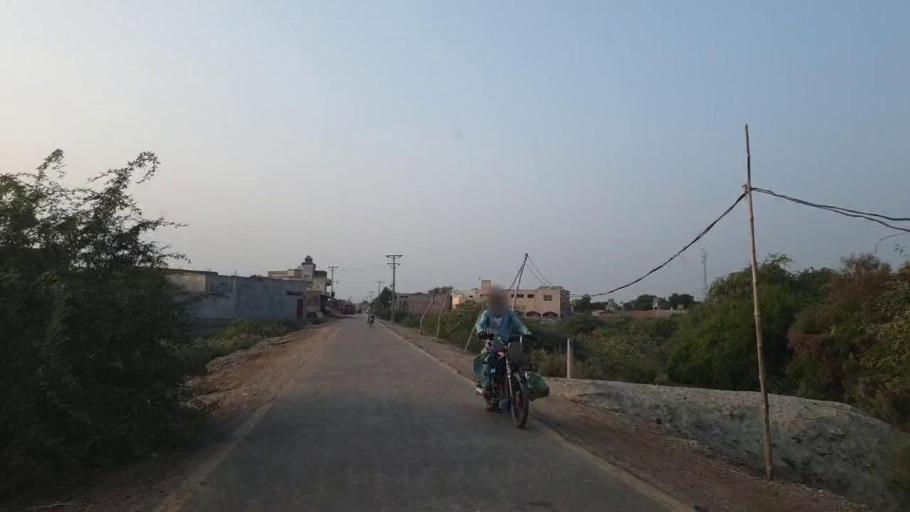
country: PK
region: Sindh
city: Tando Ghulam Ali
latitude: 25.1432
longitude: 68.9583
